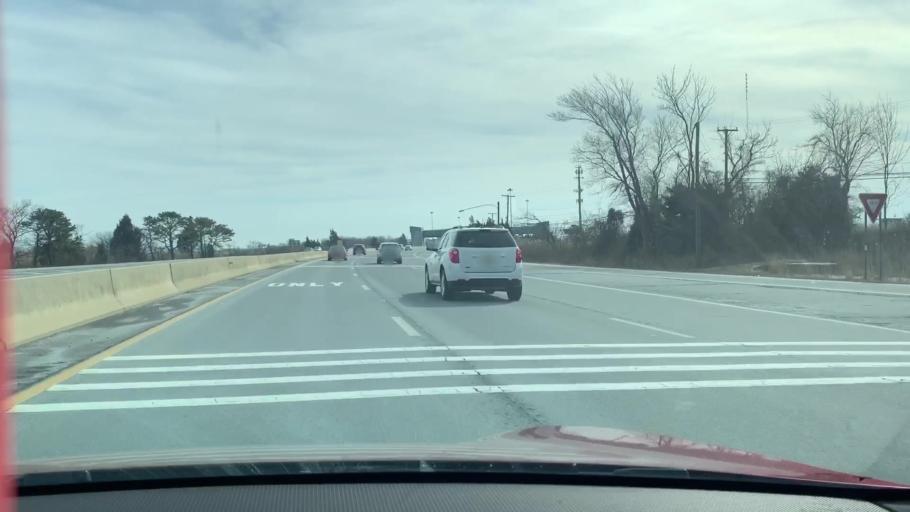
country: US
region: New Jersey
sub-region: Atlantic County
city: Pleasantville
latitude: 39.3956
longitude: -74.5129
